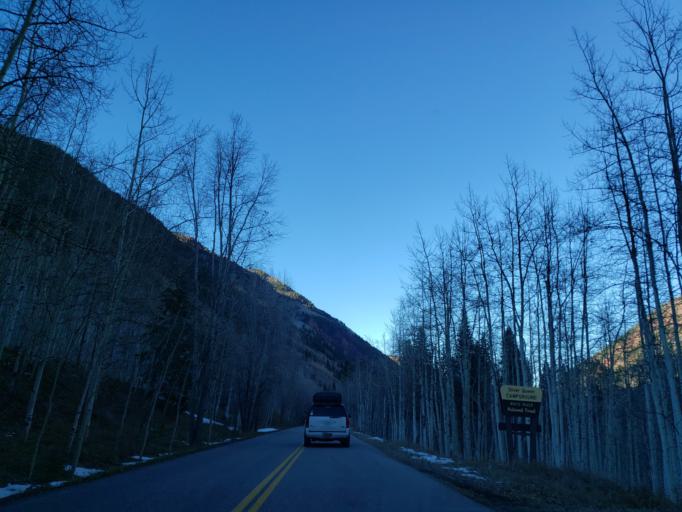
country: US
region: Colorado
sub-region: Pitkin County
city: Snowmass Village
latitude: 39.1300
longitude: -106.9024
